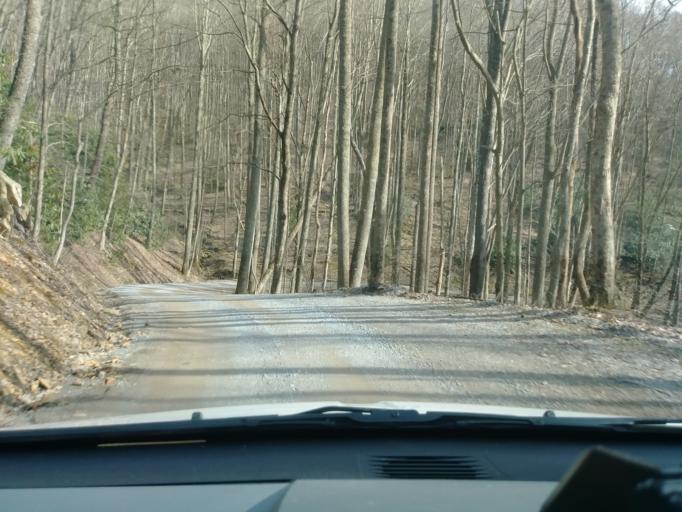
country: US
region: Tennessee
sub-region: Greene County
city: Tusculum
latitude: 36.0308
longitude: -82.7244
